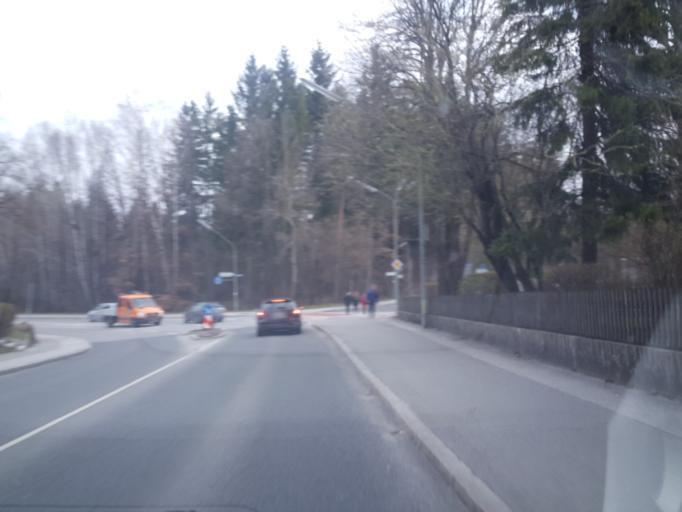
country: DE
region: Bavaria
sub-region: Upper Bavaria
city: Penzberg
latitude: 47.7581
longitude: 11.3713
